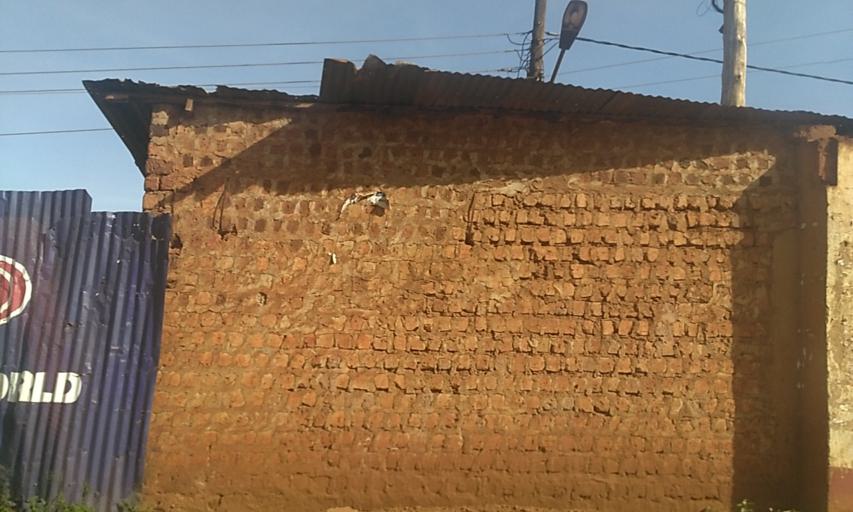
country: UG
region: Central Region
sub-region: Wakiso District
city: Kireka
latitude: 0.3590
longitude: 32.6170
